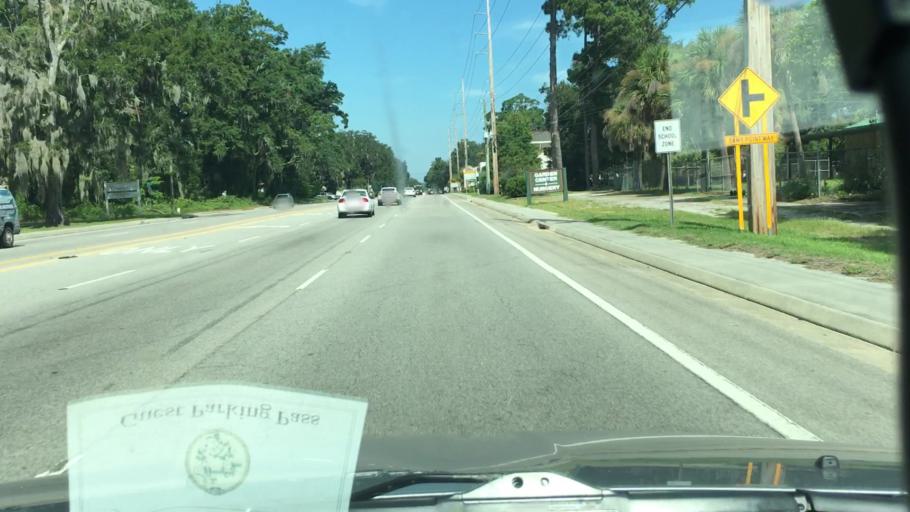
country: US
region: South Carolina
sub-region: Beaufort County
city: Beaufort
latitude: 32.4113
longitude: -80.6451
